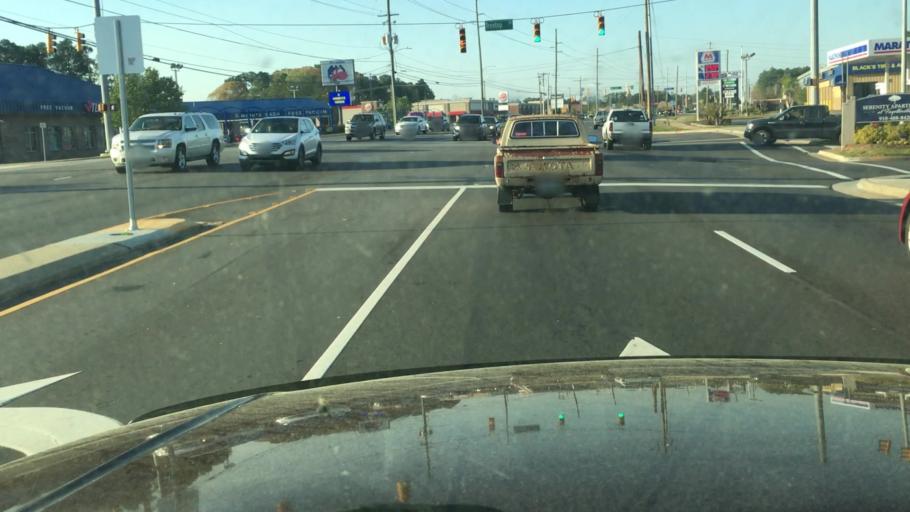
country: US
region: North Carolina
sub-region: Cumberland County
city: Fayetteville
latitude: 35.1279
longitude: -78.8791
